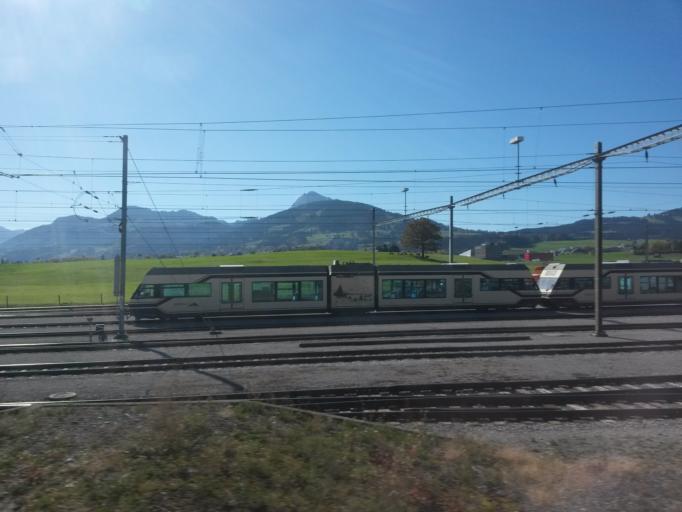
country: CH
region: Fribourg
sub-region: Gruyere District
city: Bulle
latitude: 46.6221
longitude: 7.0429
